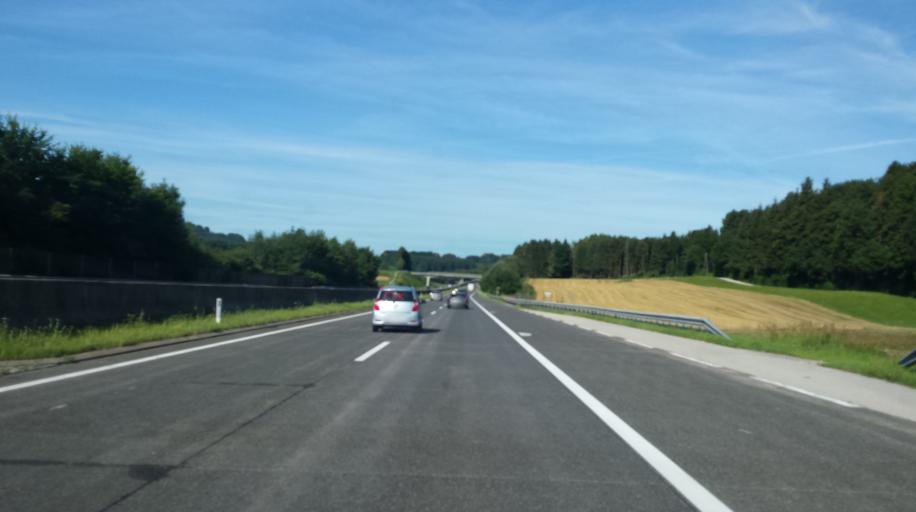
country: AT
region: Upper Austria
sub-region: Politischer Bezirk Vocklabruck
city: Seewalchen
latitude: 47.9576
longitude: 13.5594
